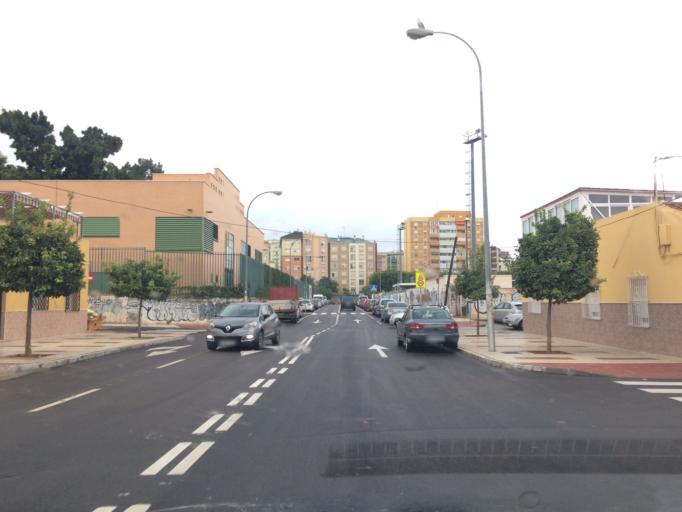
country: ES
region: Andalusia
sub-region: Provincia de Malaga
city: Malaga
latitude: 36.7192
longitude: -4.4432
